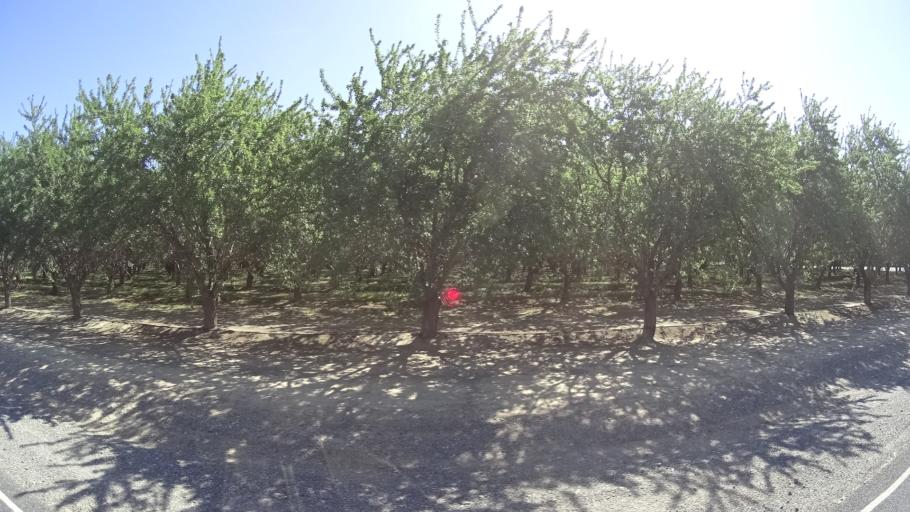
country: US
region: California
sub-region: Glenn County
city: Willows
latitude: 39.6241
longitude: -122.1041
